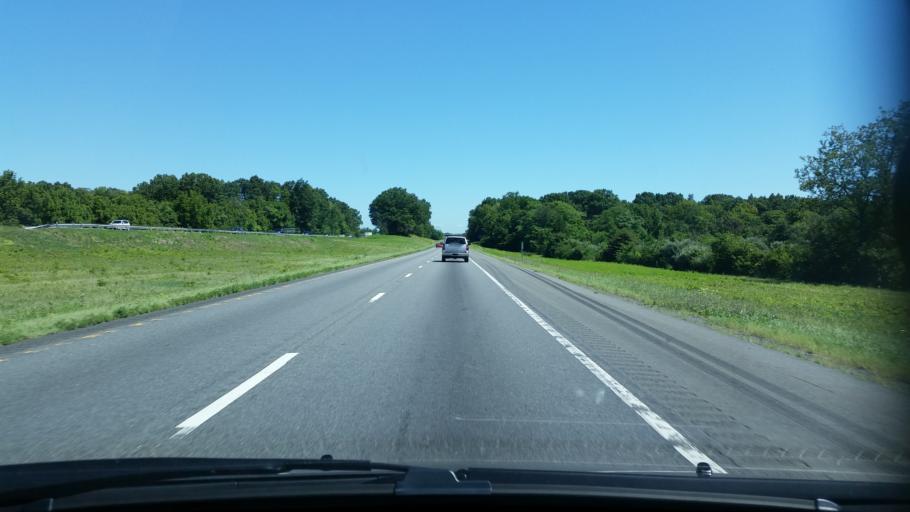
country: US
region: West Virginia
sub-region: Berkeley County
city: Inwood
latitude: 39.2761
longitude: -78.0915
